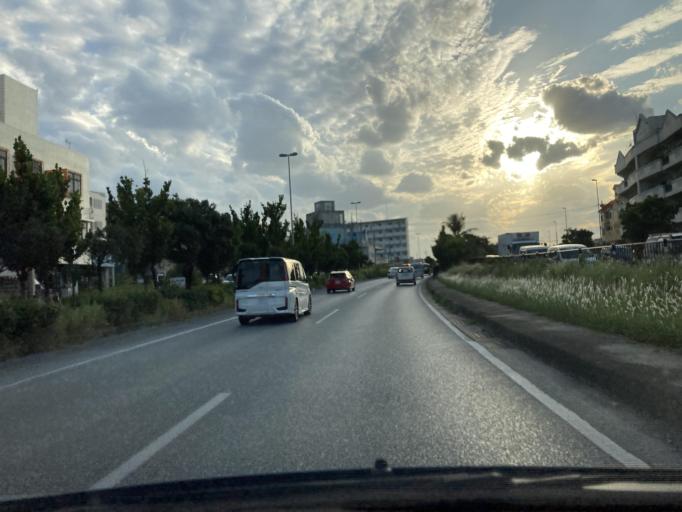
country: JP
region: Okinawa
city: Ginowan
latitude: 26.2883
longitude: 127.7531
